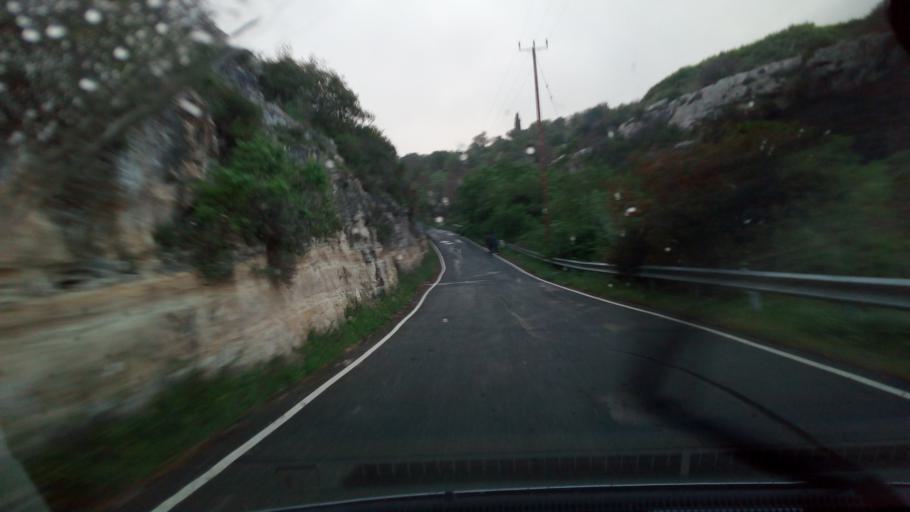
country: CY
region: Pafos
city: Polis
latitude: 34.9543
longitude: 32.4253
